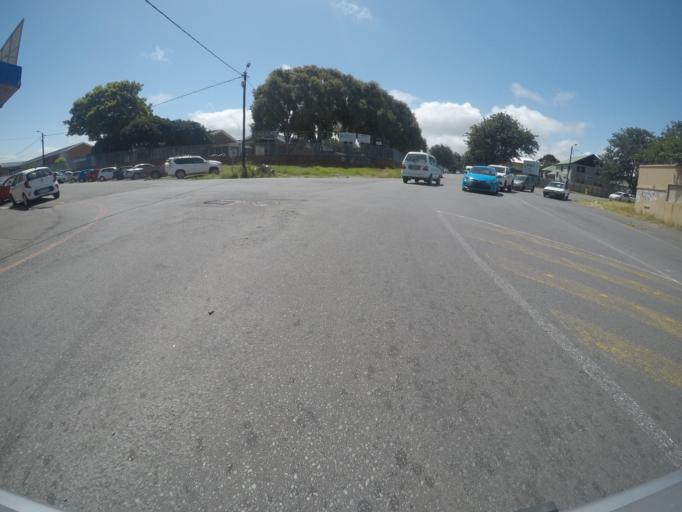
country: ZA
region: Eastern Cape
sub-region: Buffalo City Metropolitan Municipality
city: East London
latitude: -33.0067
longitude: 27.9043
